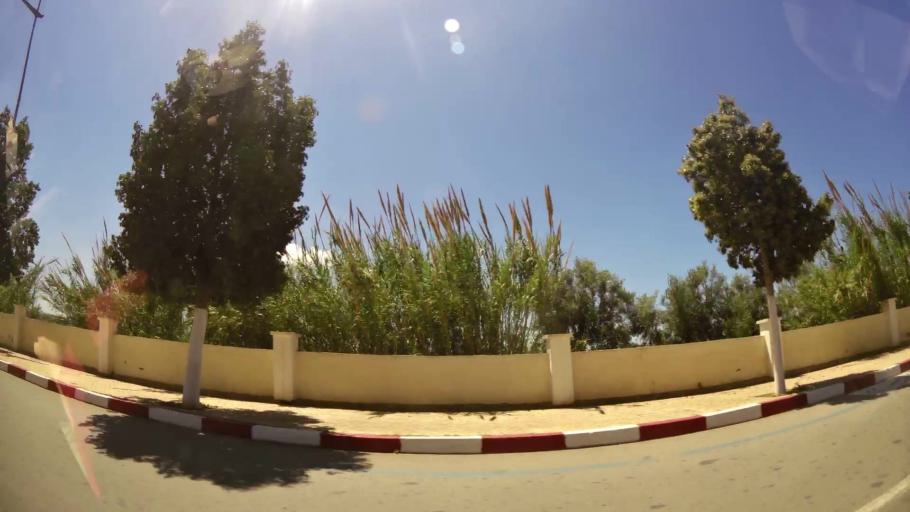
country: MA
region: Oriental
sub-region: Berkane-Taourirt
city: Madagh
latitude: 35.0729
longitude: -2.2183
